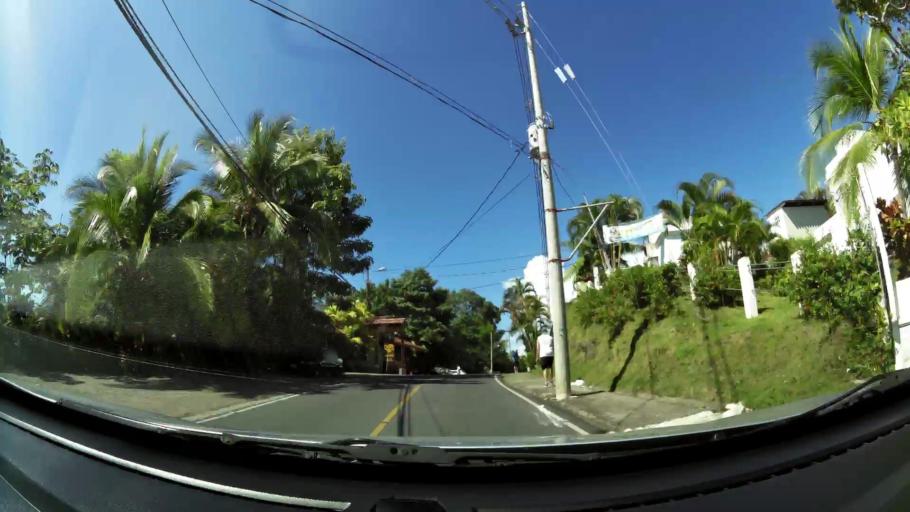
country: CR
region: Puntarenas
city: Quepos
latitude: 9.4020
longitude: -84.1530
